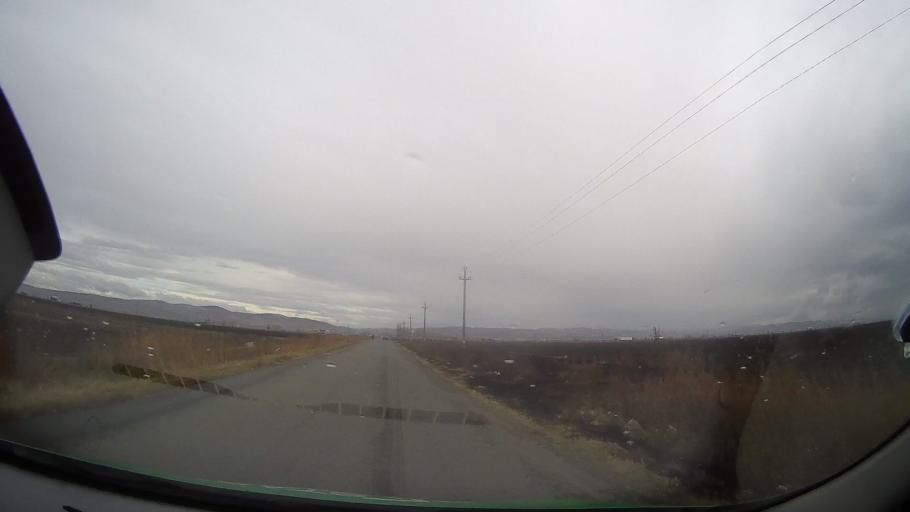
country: RO
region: Prahova
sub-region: Comuna Colceag
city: Inotesti
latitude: 44.9754
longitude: 26.3415
